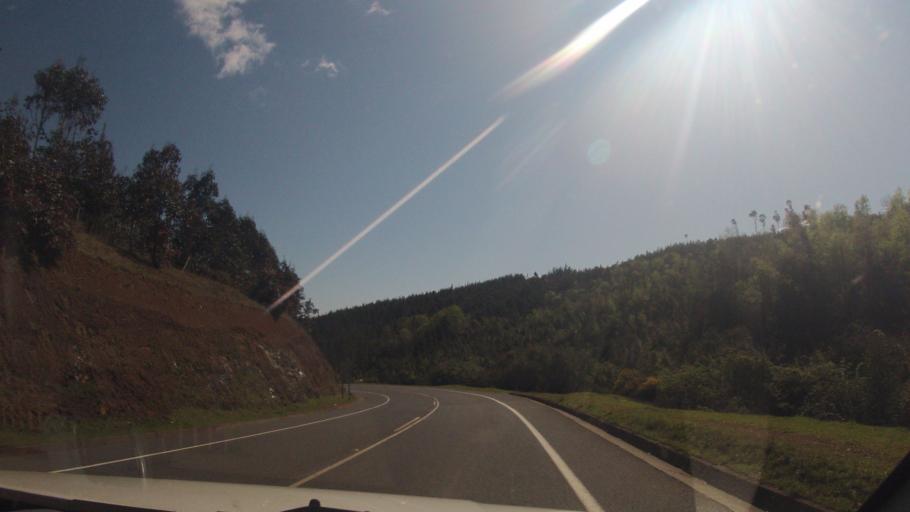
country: CL
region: Araucania
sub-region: Provincia de Malleco
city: Traiguen
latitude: -38.1712
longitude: -72.8756
